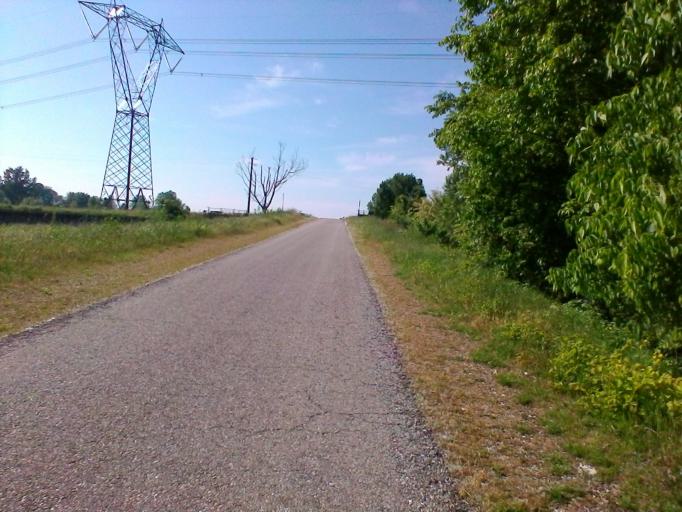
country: IT
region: Lombardy
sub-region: Provincia di Mantova
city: Marmirolo
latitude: 45.2503
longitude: 10.7307
